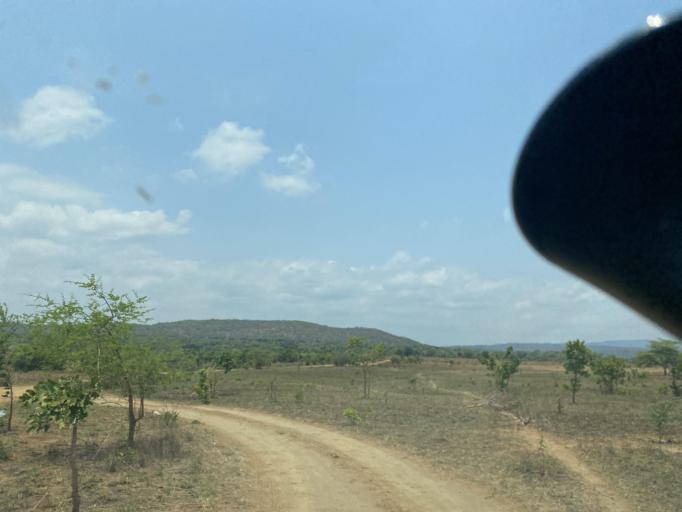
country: ZM
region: Lusaka
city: Chongwe
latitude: -15.5161
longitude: 28.8862
